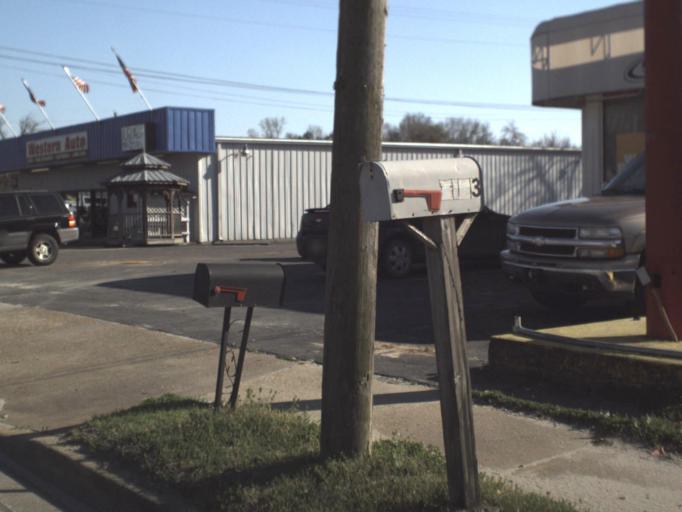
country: US
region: Florida
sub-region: Jackson County
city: Marianna
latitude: 30.7837
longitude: -85.2496
